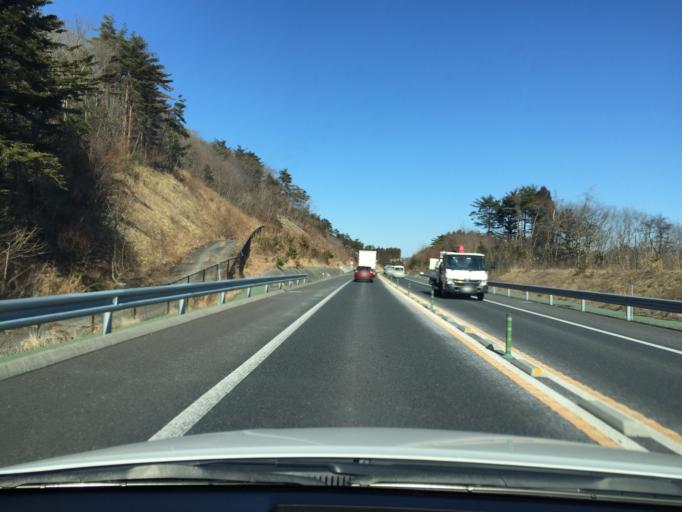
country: JP
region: Miyagi
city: Marumori
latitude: 37.7445
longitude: 140.9048
